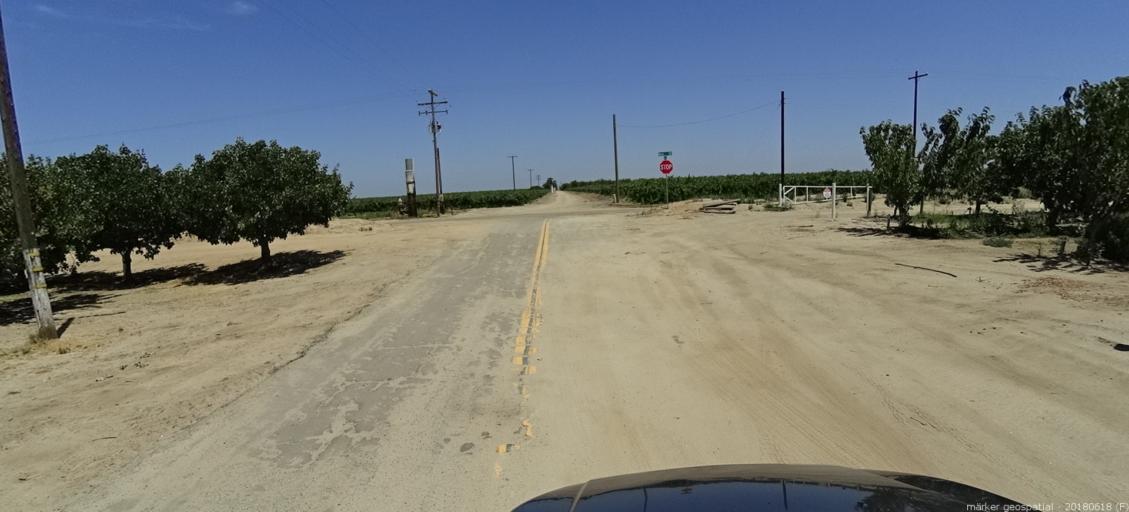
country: US
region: California
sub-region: Madera County
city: Parkwood
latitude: 36.8945
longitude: -120.1468
